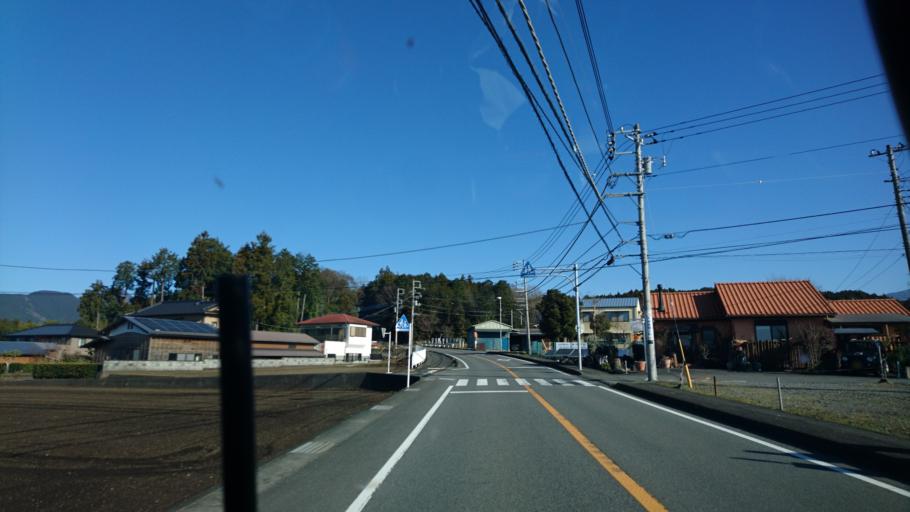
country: JP
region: Shizuoka
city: Fujinomiya
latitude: 35.2617
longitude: 138.6061
